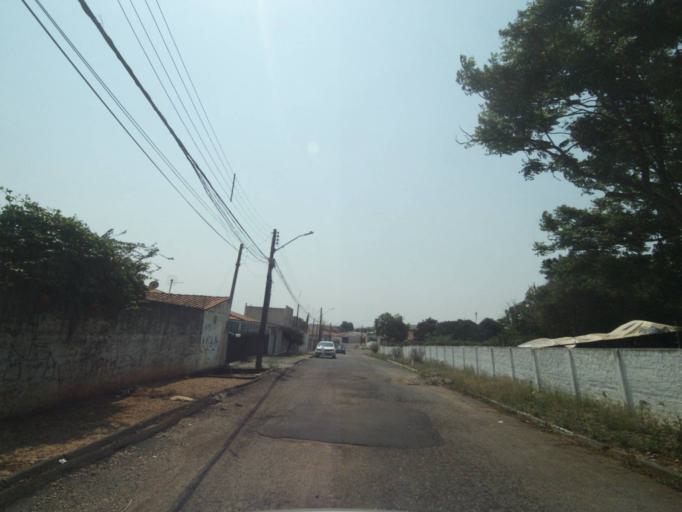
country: BR
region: Parana
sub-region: Sao Jose Dos Pinhais
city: Sao Jose dos Pinhais
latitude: -25.5439
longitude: -49.2430
